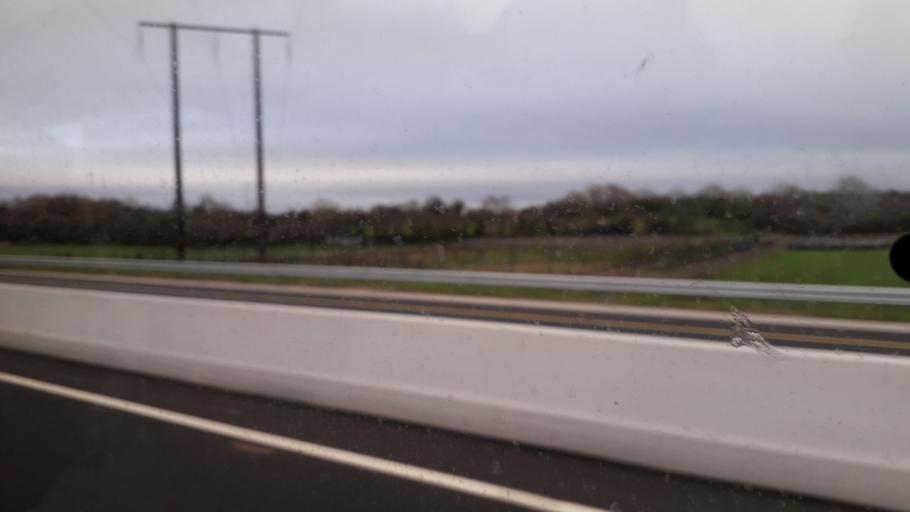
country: IE
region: Connaught
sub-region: County Galway
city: Athenry
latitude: 53.2648
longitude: -8.8153
